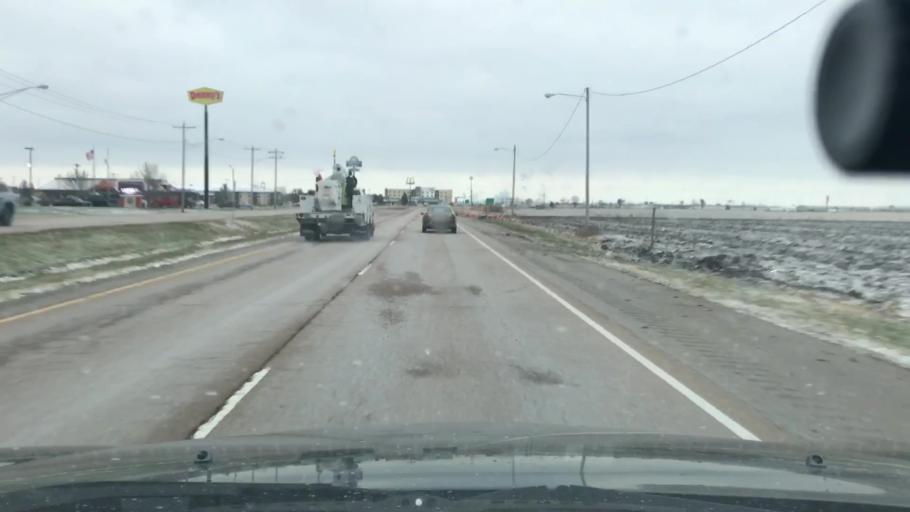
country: US
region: Illinois
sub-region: Madison County
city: Pontoon Beach
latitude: 38.7447
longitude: -90.0710
